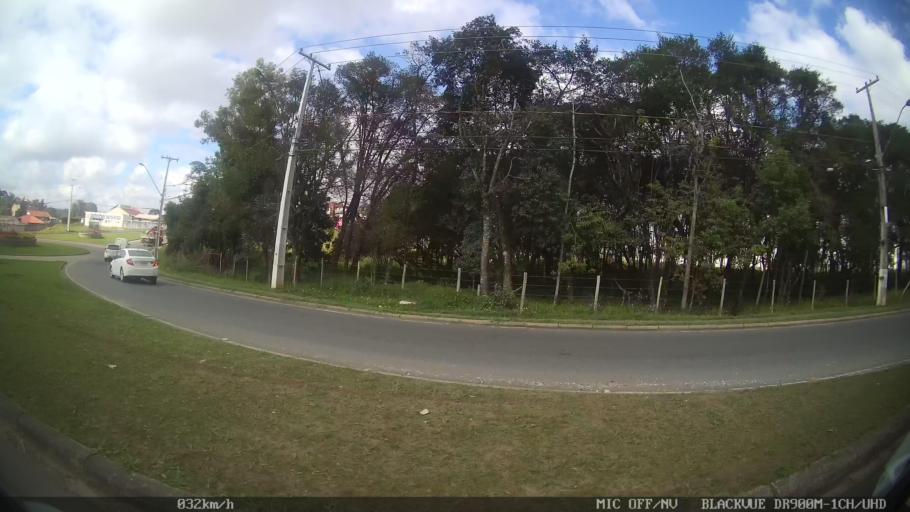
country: BR
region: Parana
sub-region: Colombo
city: Colombo
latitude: -25.3437
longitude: -49.1867
